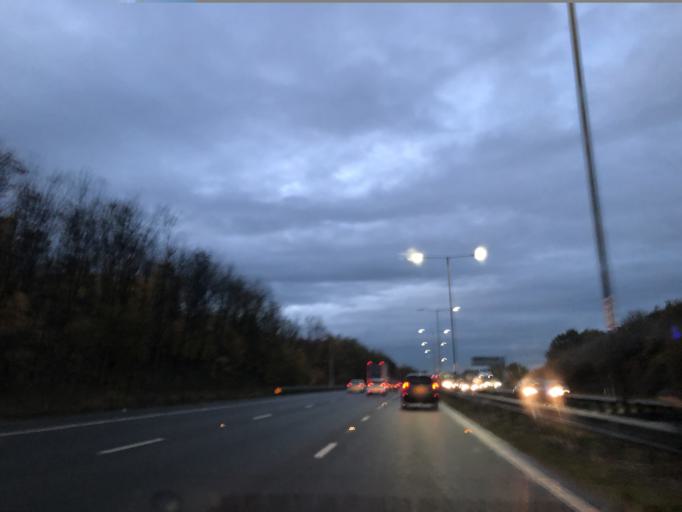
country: GB
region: England
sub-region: Solihull
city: Chelmsley Wood
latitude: 52.4924
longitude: -1.7336
